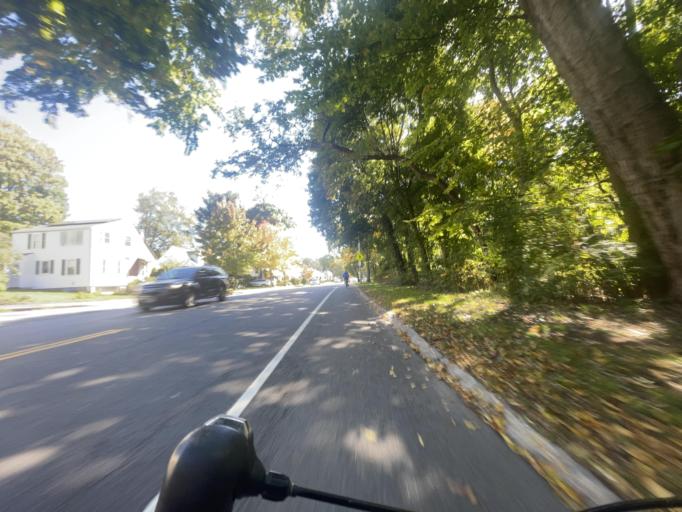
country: US
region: Massachusetts
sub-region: Norfolk County
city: Quincy
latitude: 42.2484
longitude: -71.0281
